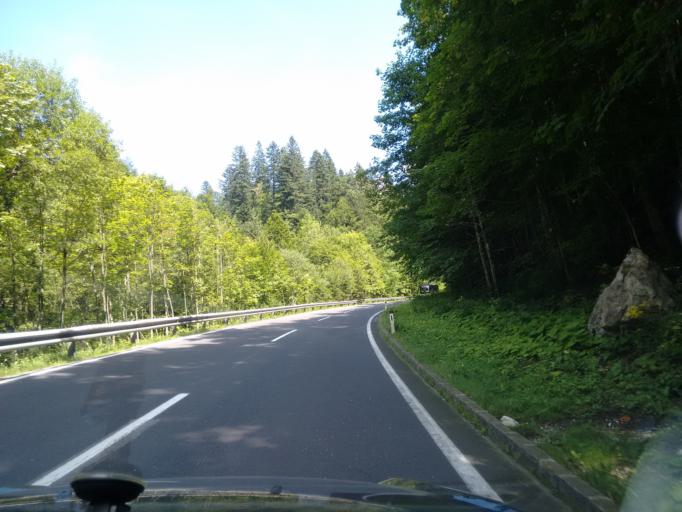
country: AT
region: Styria
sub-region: Politischer Bezirk Liezen
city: Ardning
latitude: 47.6120
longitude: 14.2876
